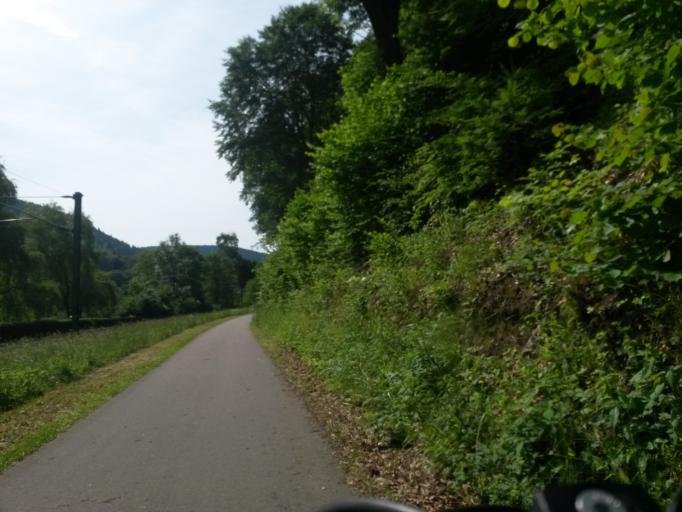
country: DE
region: Baden-Wuerttemberg
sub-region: Karlsruhe Region
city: Hofen an der Enz
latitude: 48.8204
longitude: 8.5773
